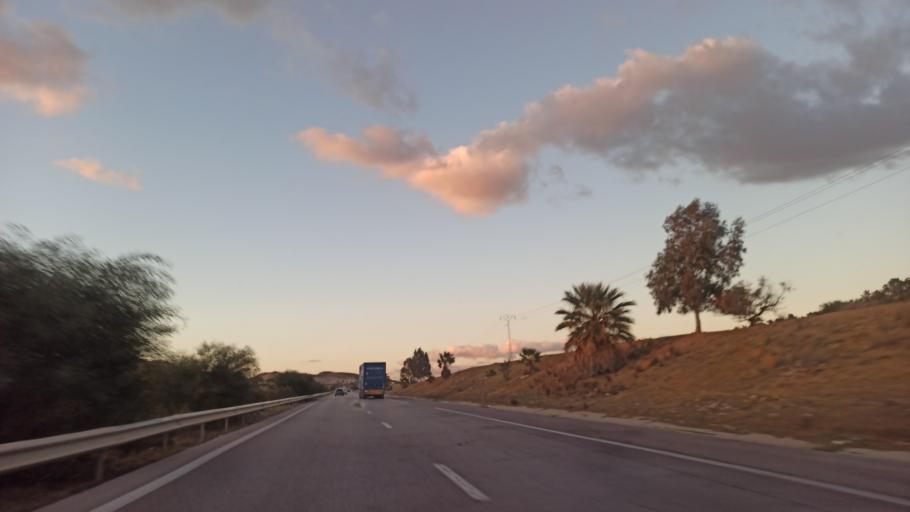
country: TN
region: Susah
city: Harqalah
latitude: 36.2210
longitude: 10.4177
